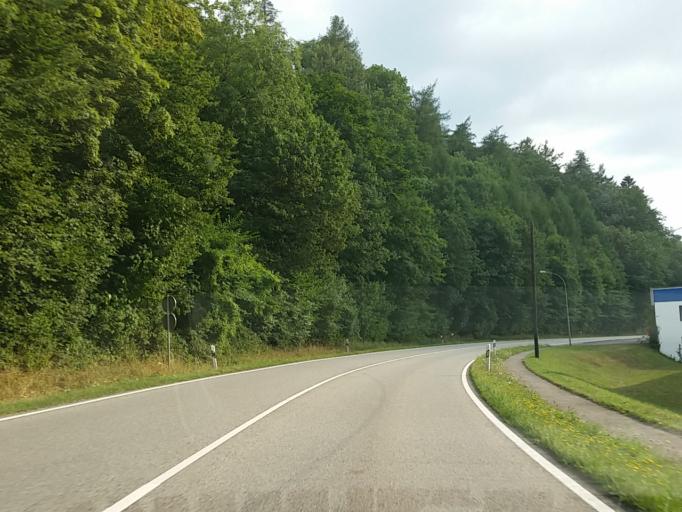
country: DE
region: Saarland
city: Wadern
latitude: 49.5333
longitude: 6.8962
